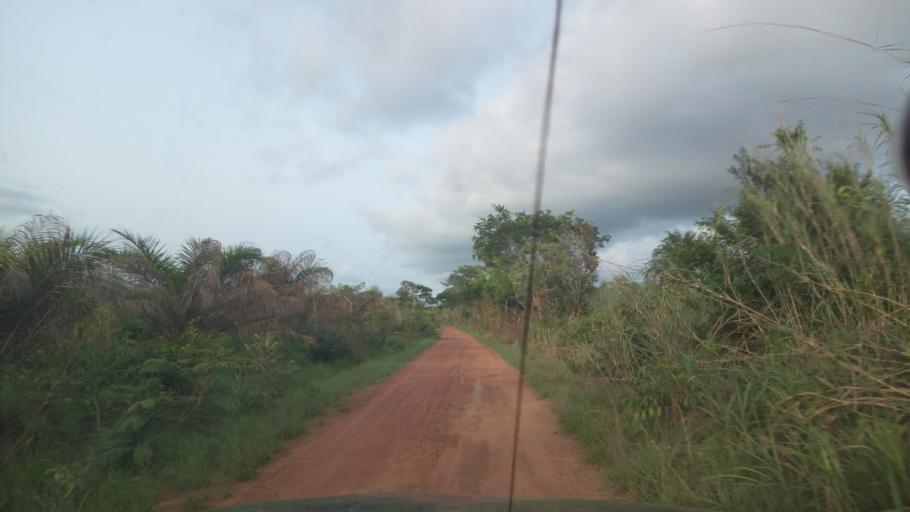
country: SL
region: Northern Province
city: Kassiri
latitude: 9.0235
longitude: -13.0543
